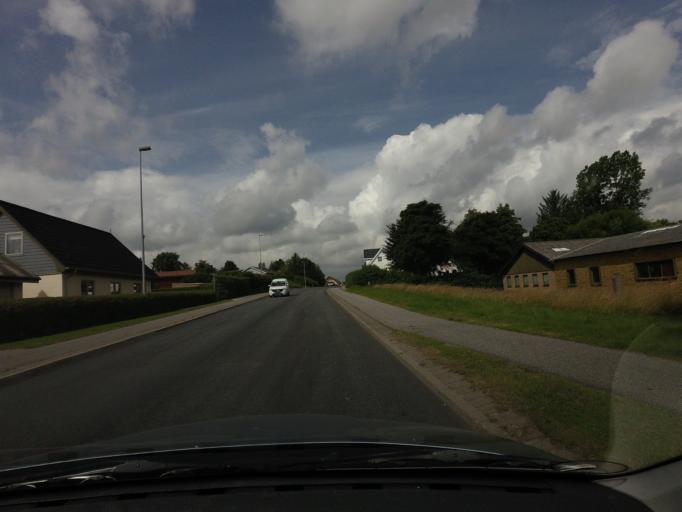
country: DK
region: North Denmark
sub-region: Hjorring Kommune
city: Tars
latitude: 57.3829
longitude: 10.1245
